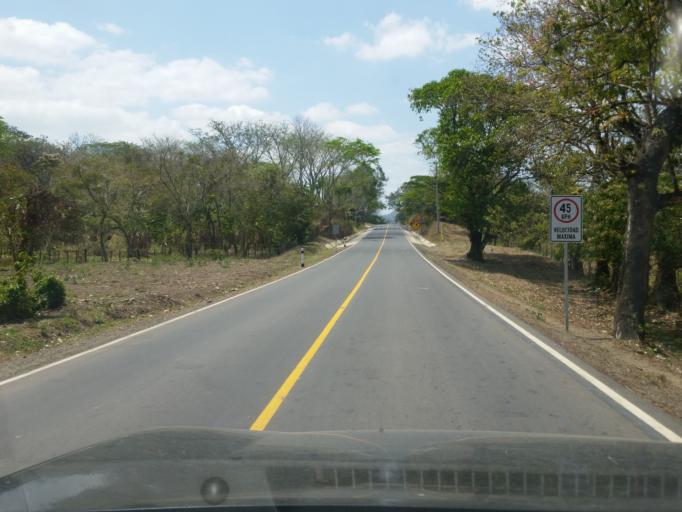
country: NI
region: Boaco
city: Boaco
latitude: 12.5634
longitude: -85.5483
